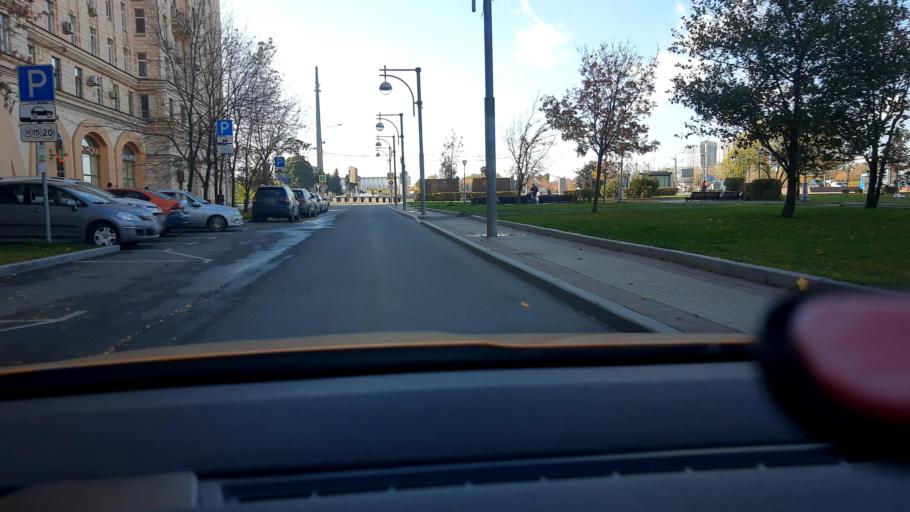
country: RU
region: Moscow
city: Vorob'yovo
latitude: 55.7358
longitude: 37.5189
